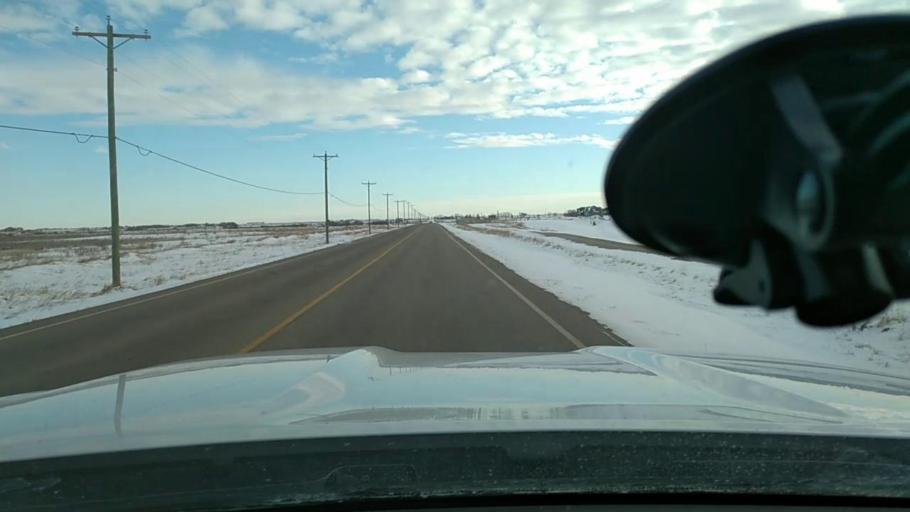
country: CA
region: Alberta
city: Chestermere
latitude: 50.9651
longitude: -113.6725
